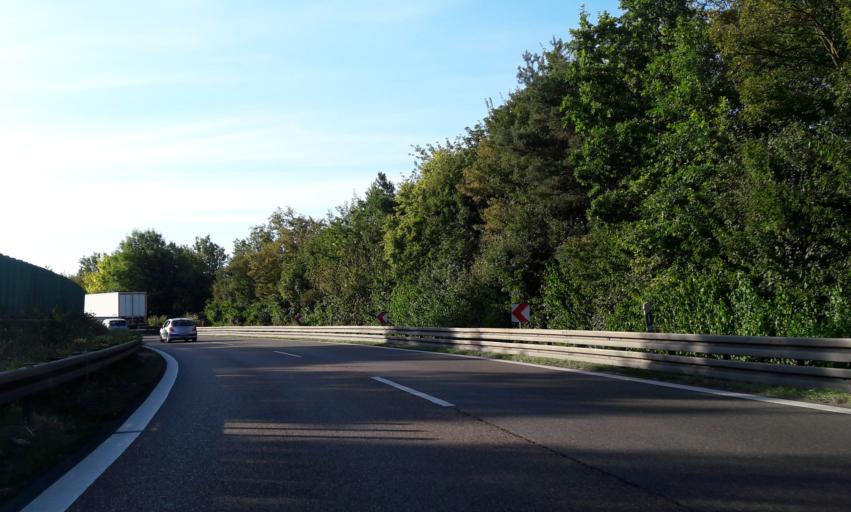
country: DE
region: Baden-Wuerttemberg
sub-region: Regierungsbezirk Stuttgart
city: Kornwestheim
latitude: 48.8410
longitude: 9.1701
